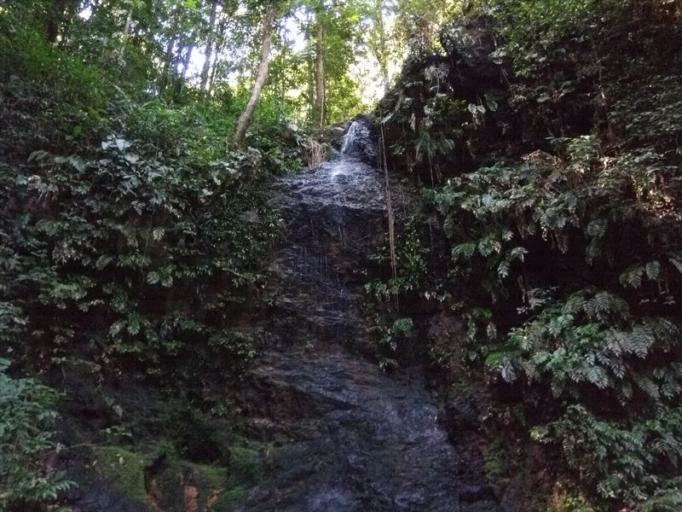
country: SR
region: Brokopondo
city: Brownsweg
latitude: 4.9543
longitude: -55.1907
